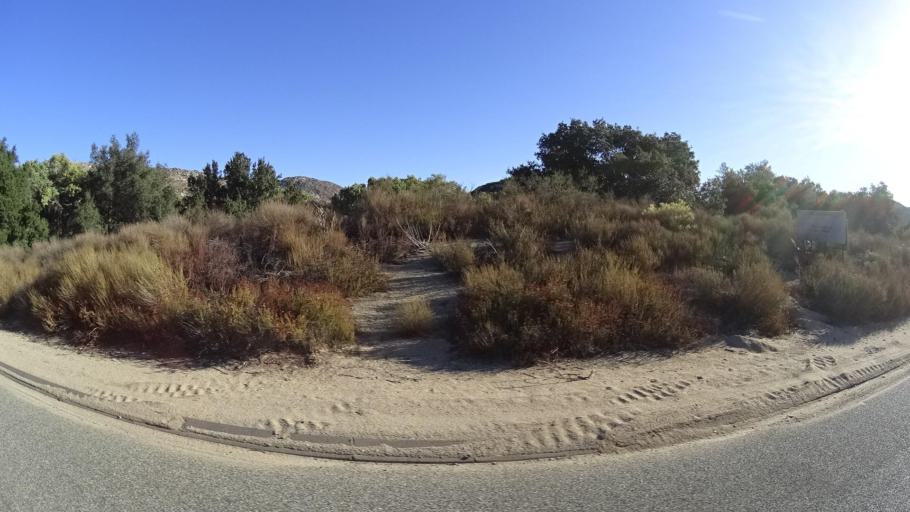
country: MX
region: Baja California
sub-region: Tecate
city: Hacienda Tecate
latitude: 32.5893
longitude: -116.5205
